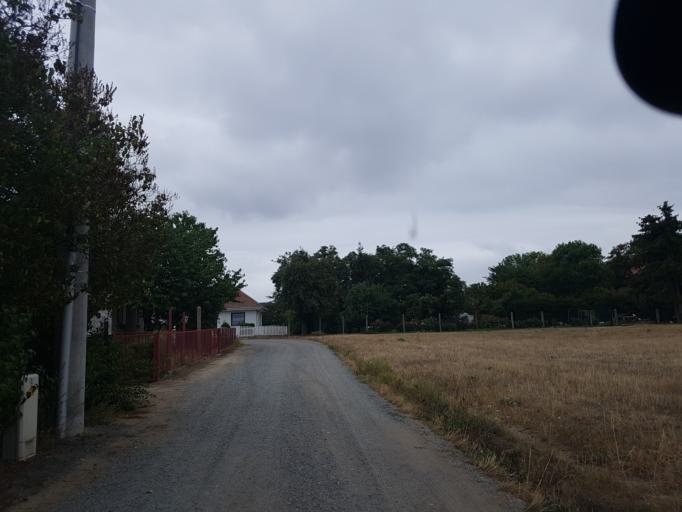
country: DE
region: Saxony-Anhalt
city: Nudersdorf
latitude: 51.8732
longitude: 12.5399
